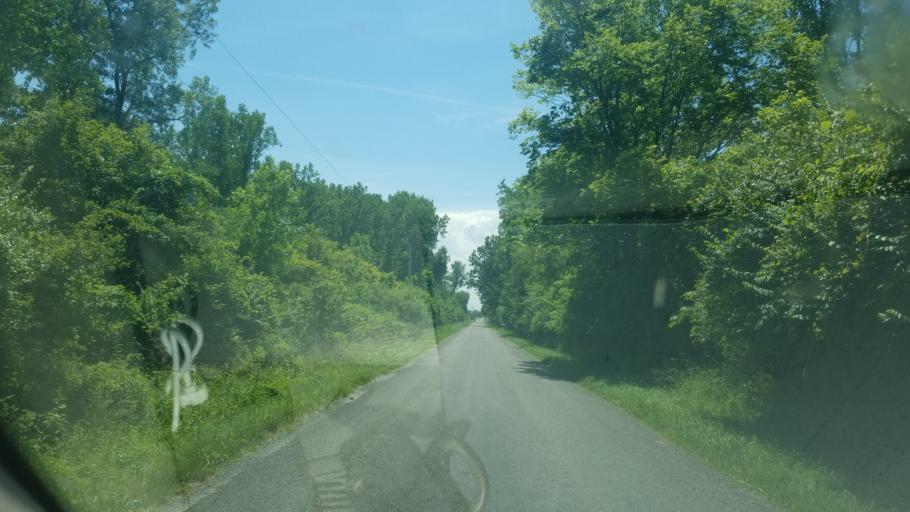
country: US
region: Ohio
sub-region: Hancock County
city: Findlay
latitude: 41.0040
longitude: -83.6363
